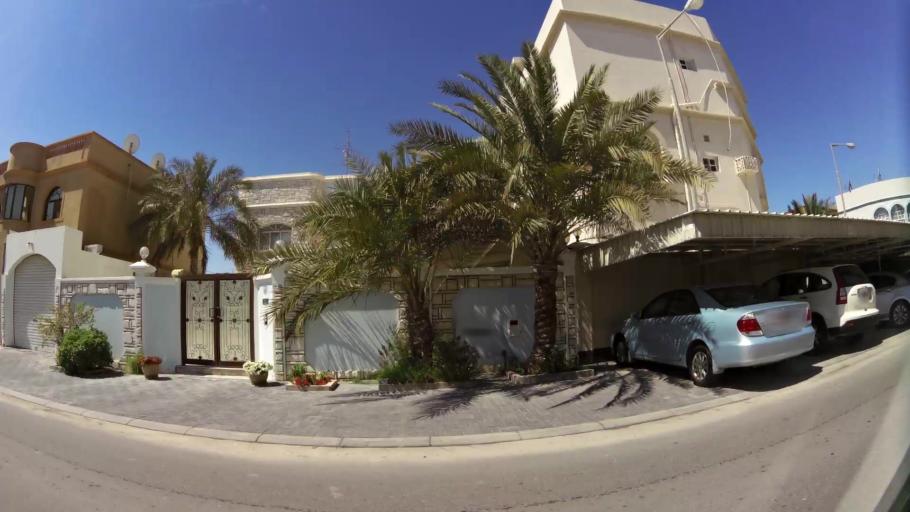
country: BH
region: Muharraq
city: Al Muharraq
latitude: 26.2726
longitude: 50.6054
